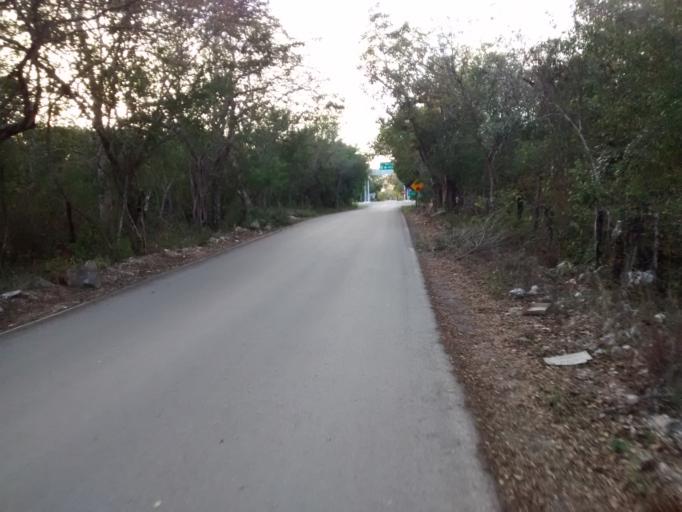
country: MX
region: Yucatan
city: Valladolid
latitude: 20.6813
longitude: -88.1639
